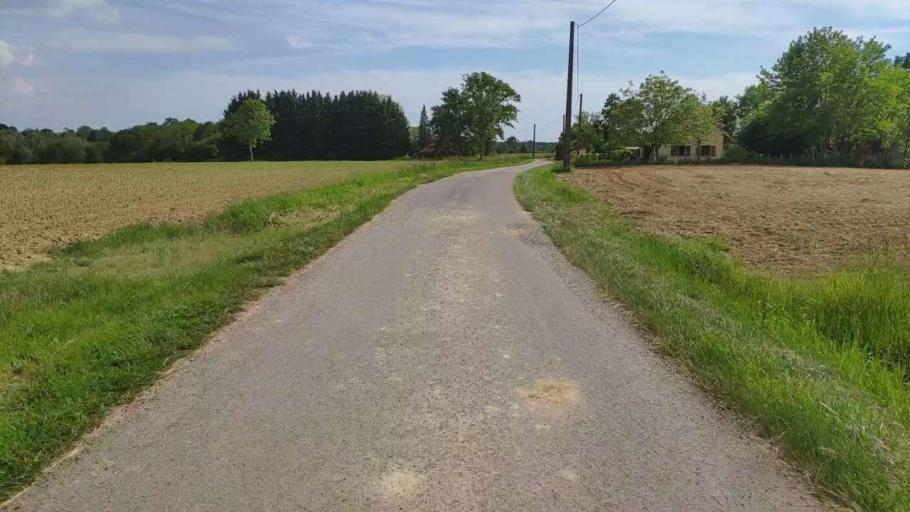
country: FR
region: Franche-Comte
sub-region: Departement du Jura
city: Bletterans
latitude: 46.8122
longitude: 5.3858
